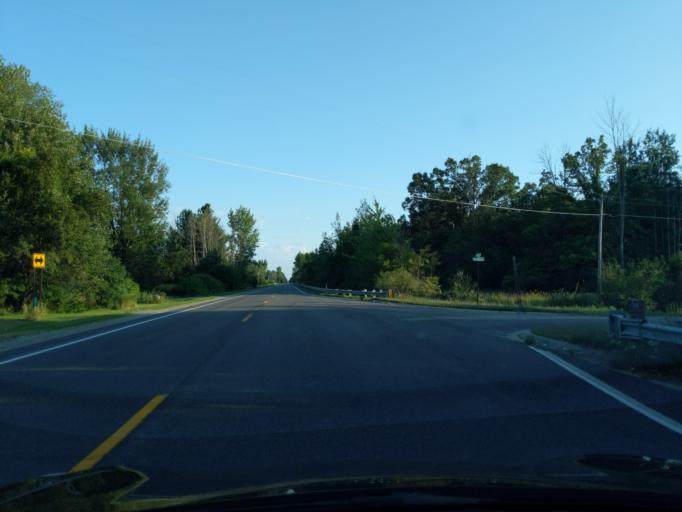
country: US
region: Michigan
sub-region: Midland County
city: Midland
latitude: 43.5533
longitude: -84.3697
